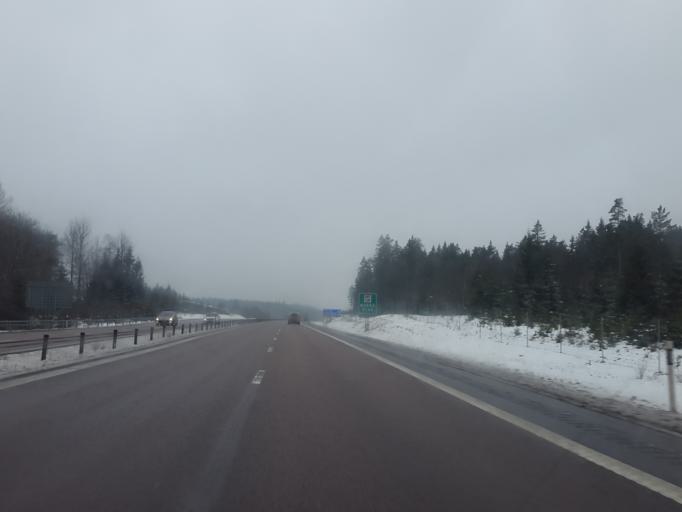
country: SE
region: Vaestra Goetaland
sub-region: Boras Kommun
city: Dalsjofors
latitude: 57.8031
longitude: 13.1676
